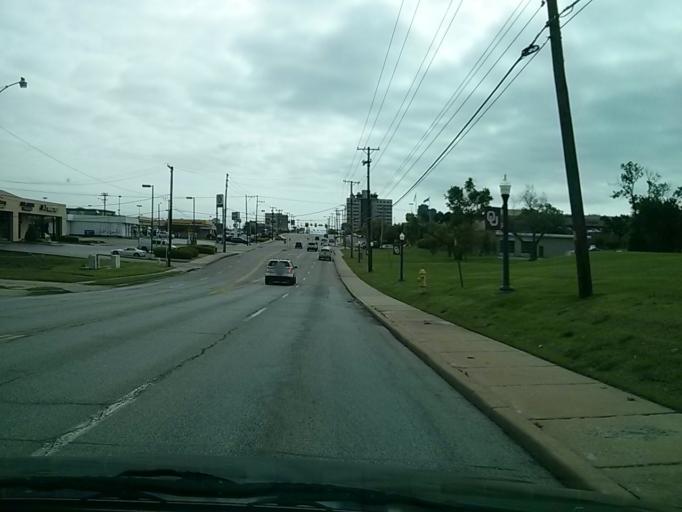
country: US
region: Oklahoma
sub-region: Tulsa County
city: Tulsa
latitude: 36.1043
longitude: -95.9244
